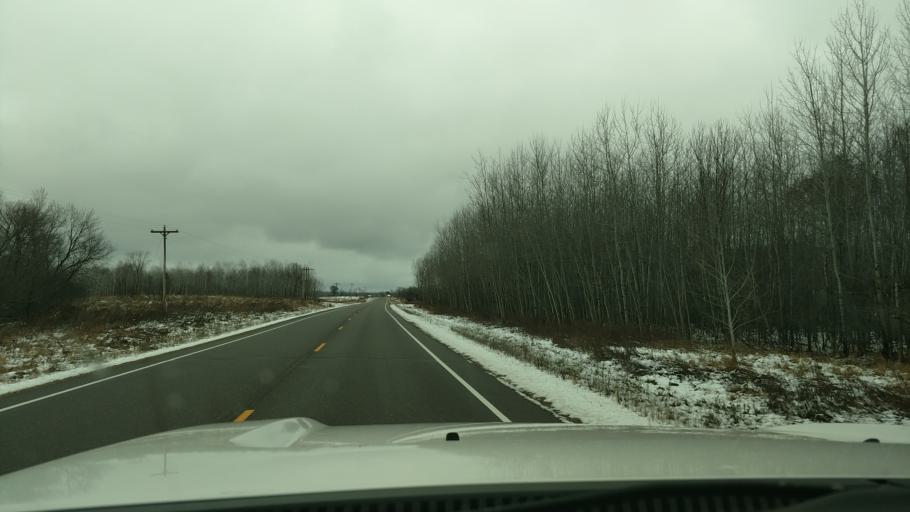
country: US
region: Wisconsin
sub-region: Dunn County
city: Colfax
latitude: 45.1381
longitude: -91.7831
